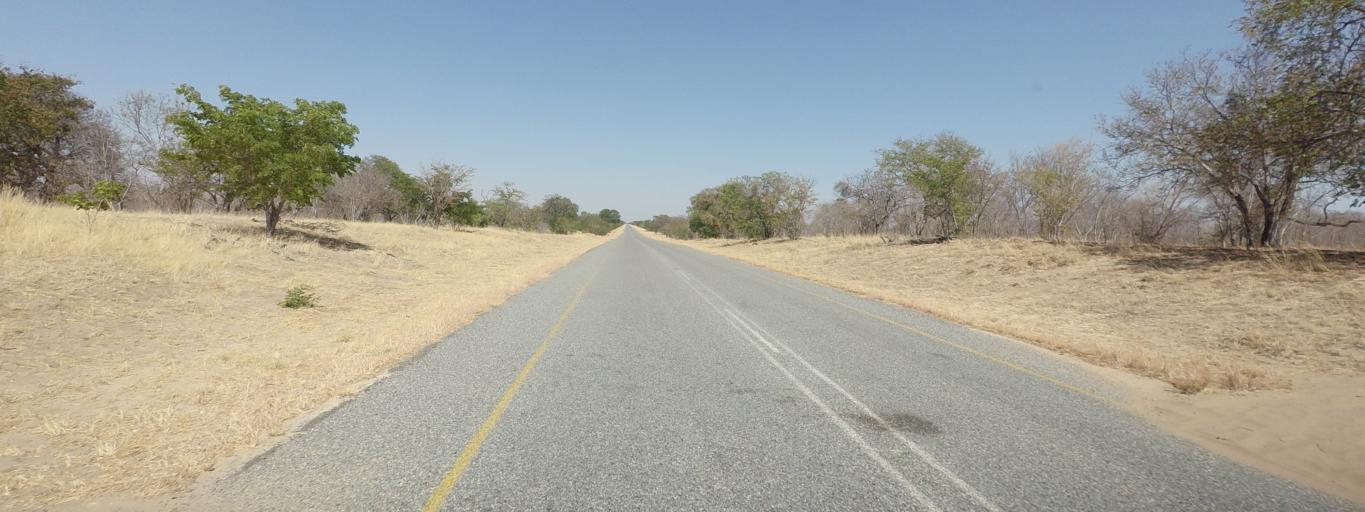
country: BW
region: North West
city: Kasane
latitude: -17.9217
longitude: 24.9995
